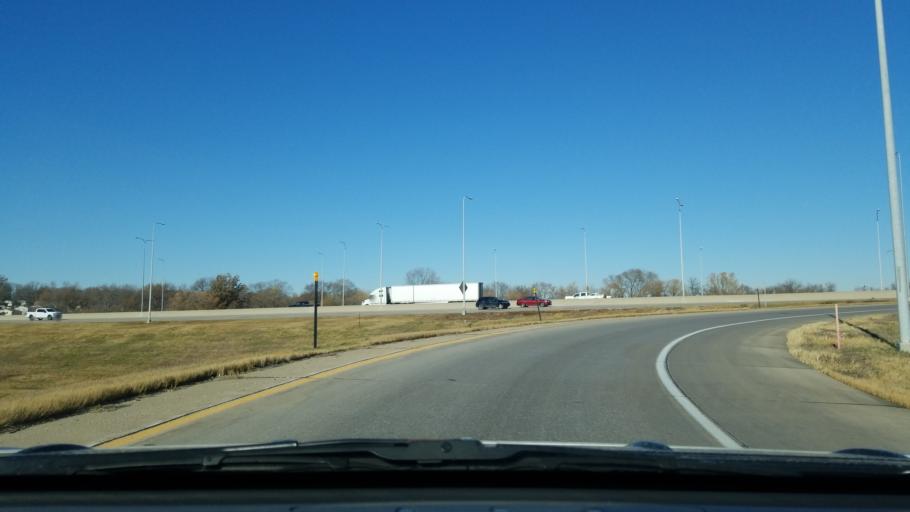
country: US
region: Nebraska
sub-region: Douglas County
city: Ralston
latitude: 41.2229
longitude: -96.0442
